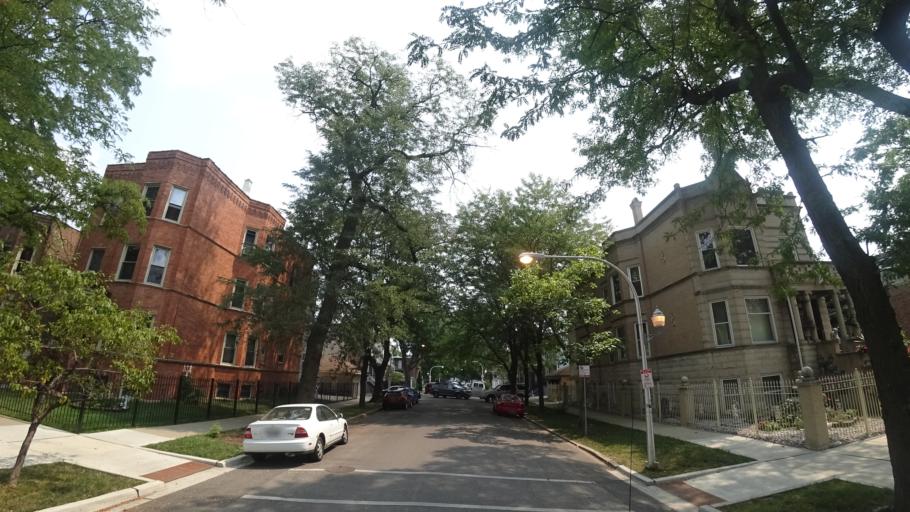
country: US
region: Illinois
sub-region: Cook County
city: Cicero
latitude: 41.8451
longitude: -87.7296
